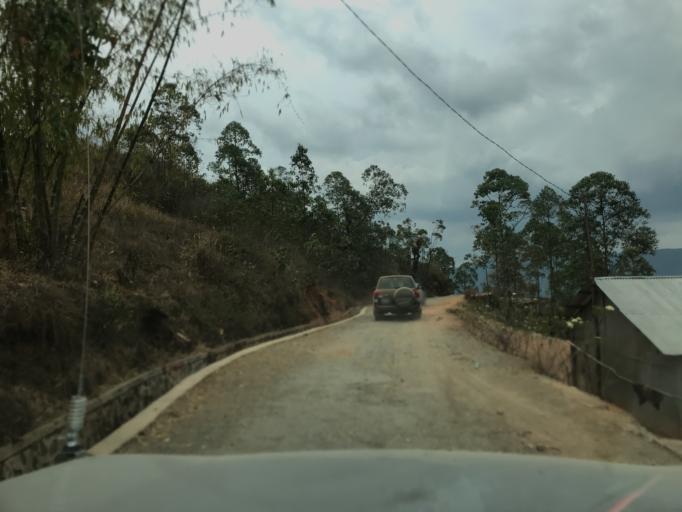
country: TL
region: Ermera
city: Gleno
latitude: -8.8381
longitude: 125.4385
